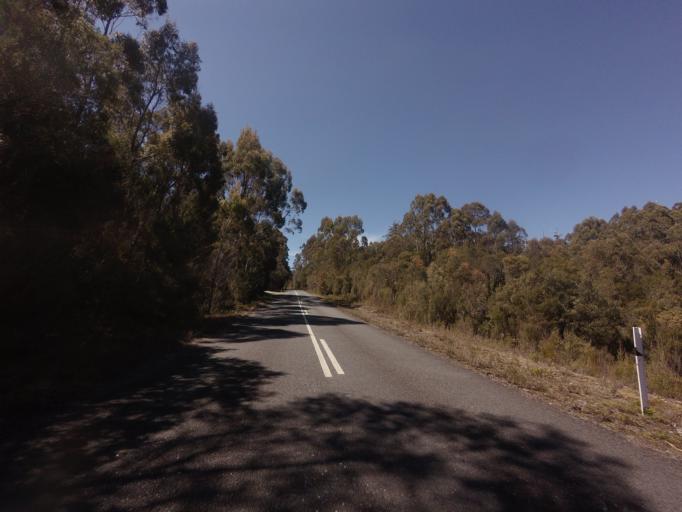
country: AU
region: Tasmania
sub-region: West Coast
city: Queenstown
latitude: -42.7745
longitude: 146.0399
